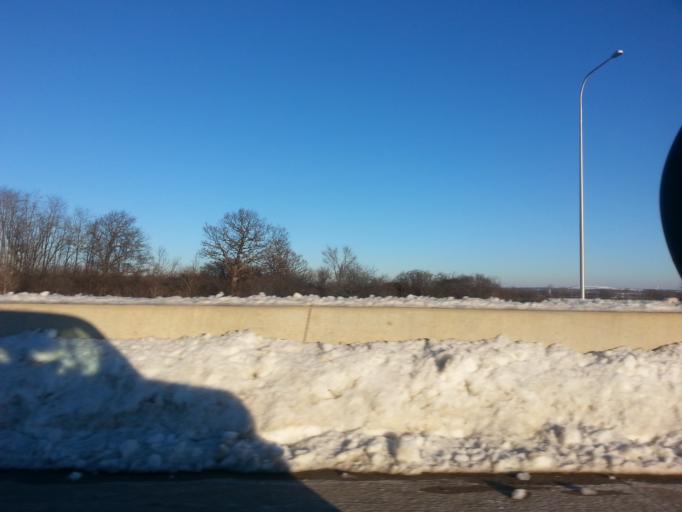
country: US
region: Wisconsin
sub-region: Kenosha County
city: Pleasant Prairie
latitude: 42.4924
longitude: -87.9491
